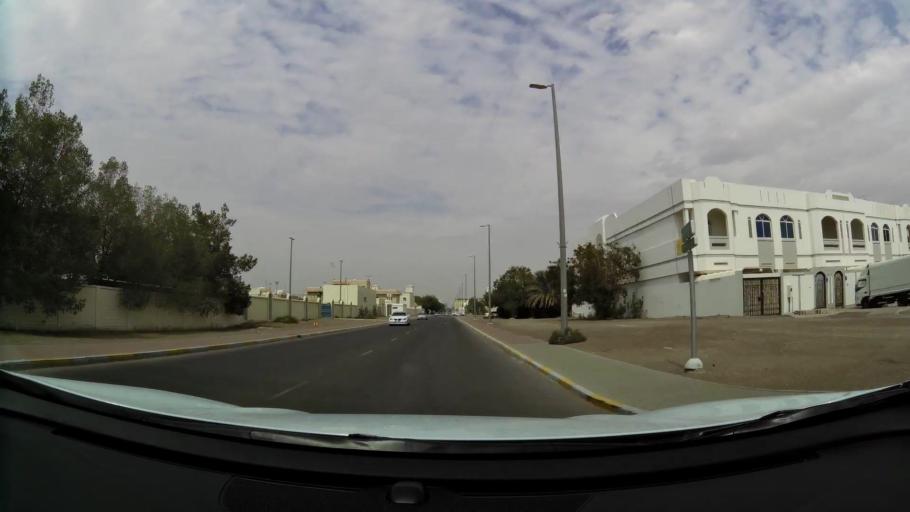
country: AE
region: Abu Dhabi
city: Al Ain
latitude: 24.2156
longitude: 55.7841
